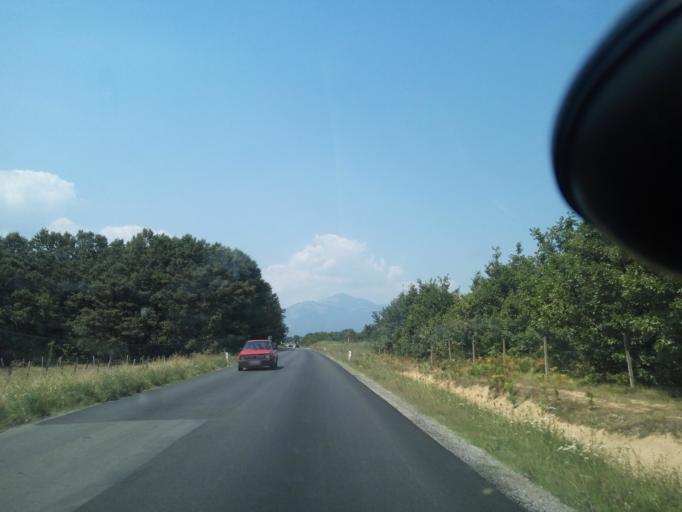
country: XK
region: Gjakova
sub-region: Komuna e Decanit
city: Gllogjan
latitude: 42.4557
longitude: 20.3561
